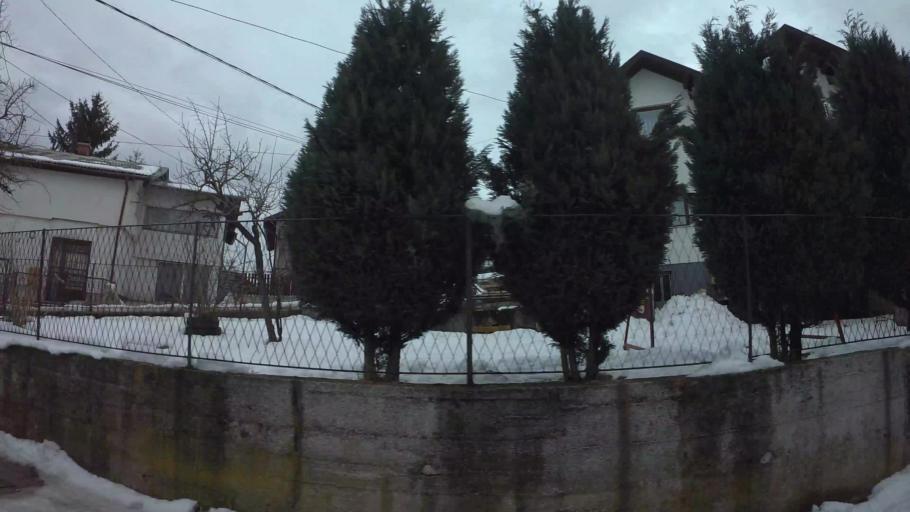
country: BA
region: Federation of Bosnia and Herzegovina
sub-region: Kanton Sarajevo
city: Sarajevo
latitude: 43.8673
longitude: 18.3217
